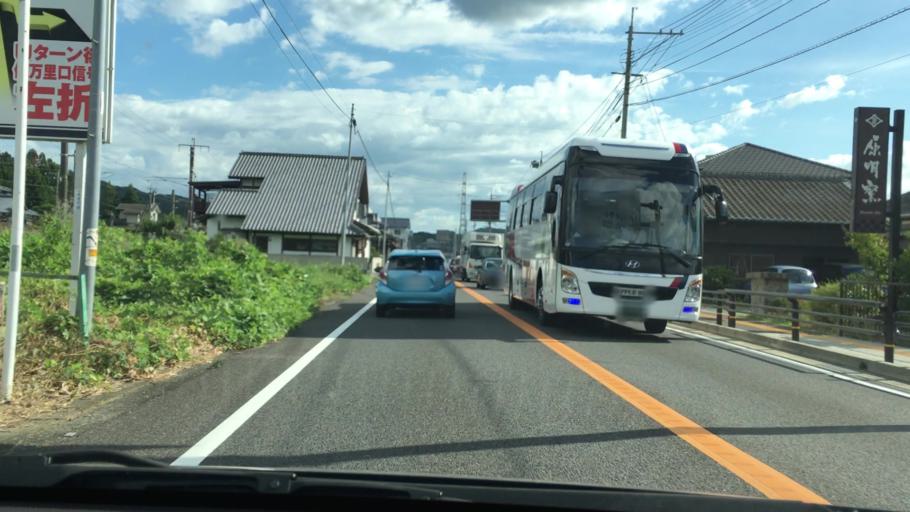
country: JP
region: Saga Prefecture
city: Imaricho-ko
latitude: 33.1838
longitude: 129.8541
